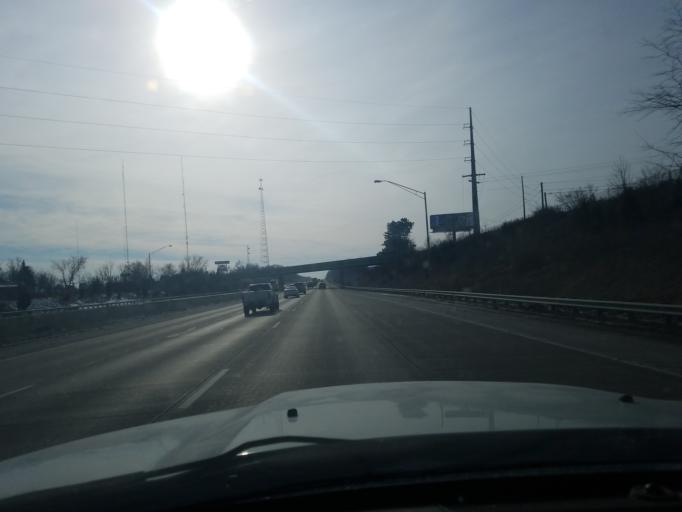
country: US
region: Indiana
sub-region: Allen County
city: Fort Wayne
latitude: 41.1178
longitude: -85.1914
